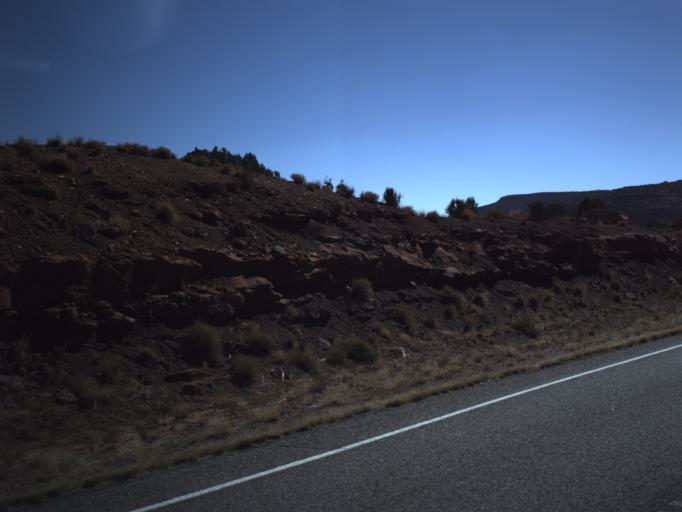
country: US
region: Utah
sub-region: San Juan County
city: Blanding
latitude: 37.6213
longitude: -110.0847
